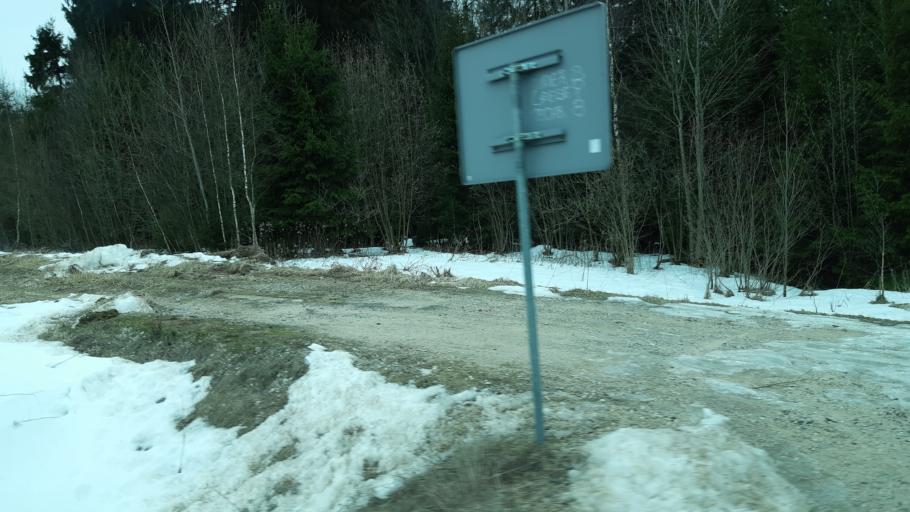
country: LT
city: Virbalis
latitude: 54.3807
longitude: 22.8174
